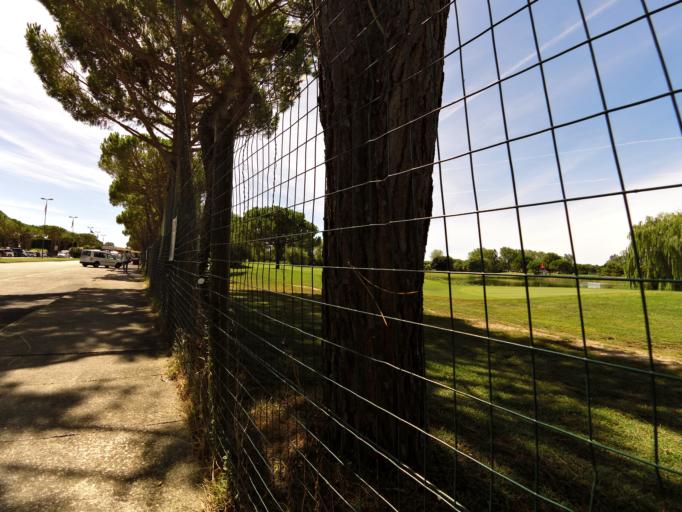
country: IT
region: Veneto
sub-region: Provincia di Venezia
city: Caorle
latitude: 45.5743
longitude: 12.8107
